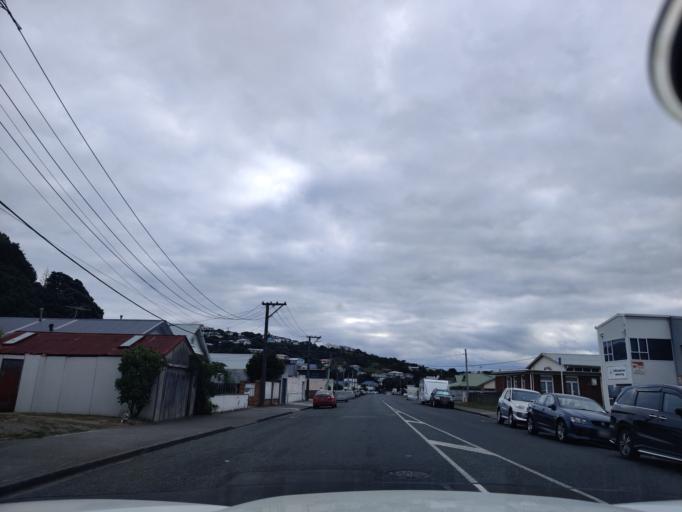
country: NZ
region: Wellington
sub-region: Wellington City
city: Wellington
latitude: -41.3138
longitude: 174.8144
